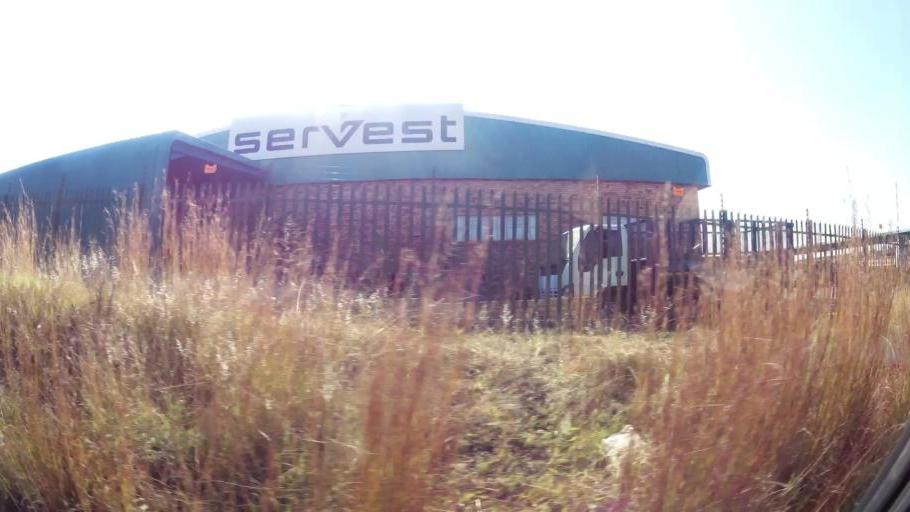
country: ZA
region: Gauteng
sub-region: West Rand District Municipality
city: Muldersdriseloop
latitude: -26.0326
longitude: 27.9449
